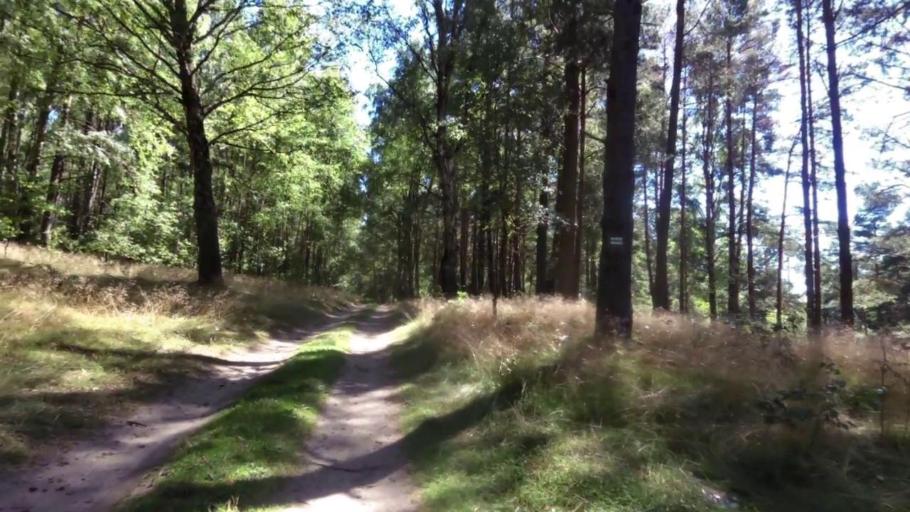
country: PL
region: West Pomeranian Voivodeship
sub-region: Powiat szczecinecki
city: Bialy Bor
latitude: 53.8487
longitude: 16.8707
